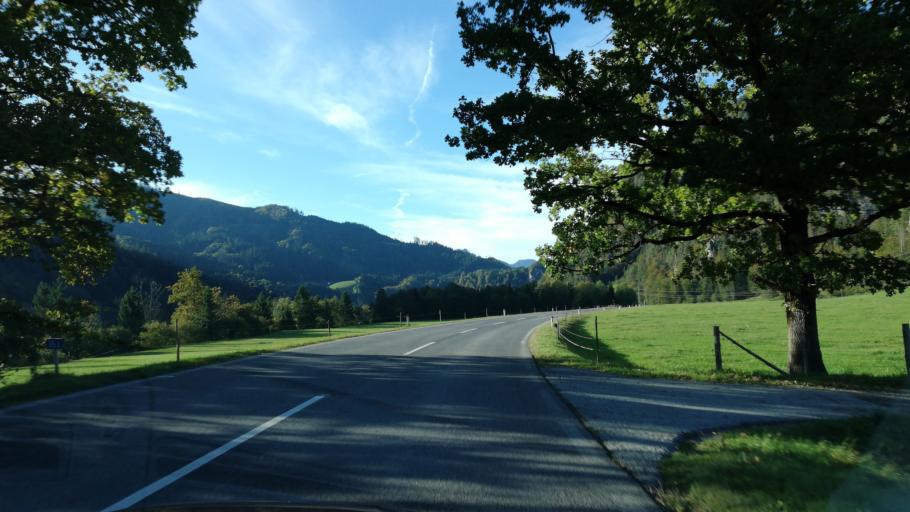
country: AT
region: Styria
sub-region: Politischer Bezirk Liezen
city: Landl
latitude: 47.6891
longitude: 14.6978
